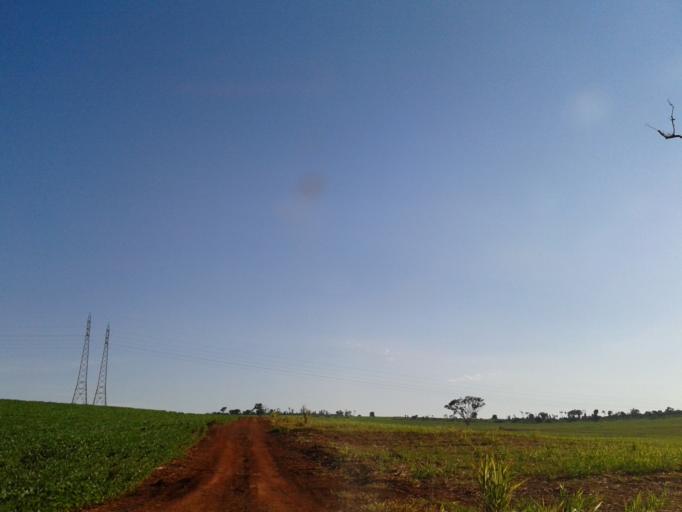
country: BR
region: Minas Gerais
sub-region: Centralina
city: Centralina
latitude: -18.6783
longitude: -49.2760
